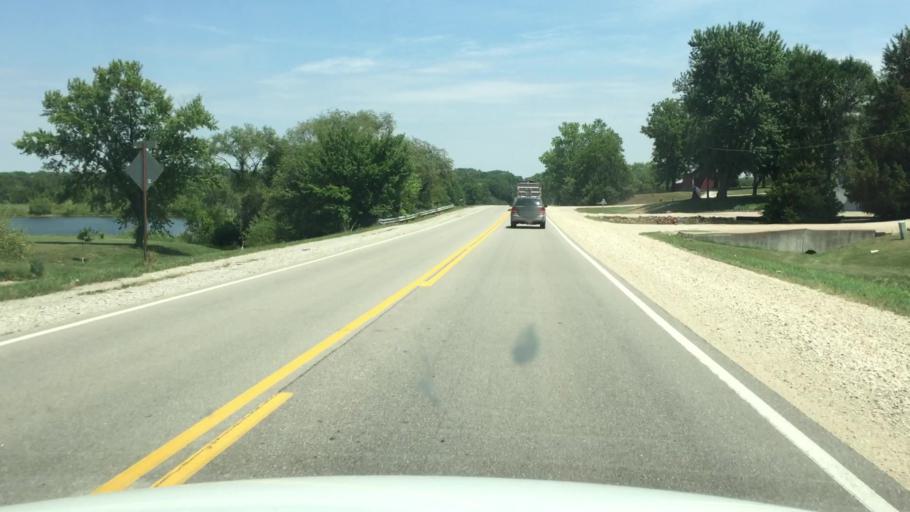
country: US
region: Kansas
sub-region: Shawnee County
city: Topeka
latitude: 38.9861
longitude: -95.5842
